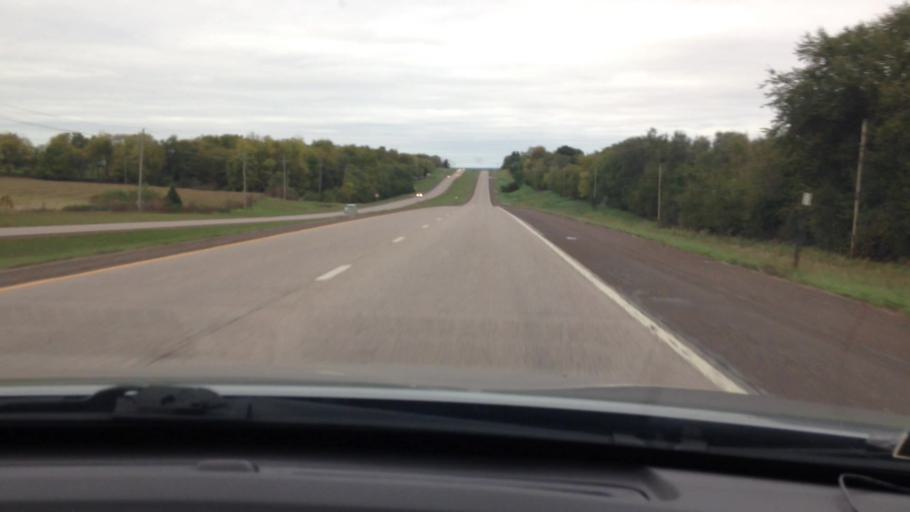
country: US
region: Kansas
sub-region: Leavenworth County
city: Lansing
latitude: 39.1949
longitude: -94.9002
